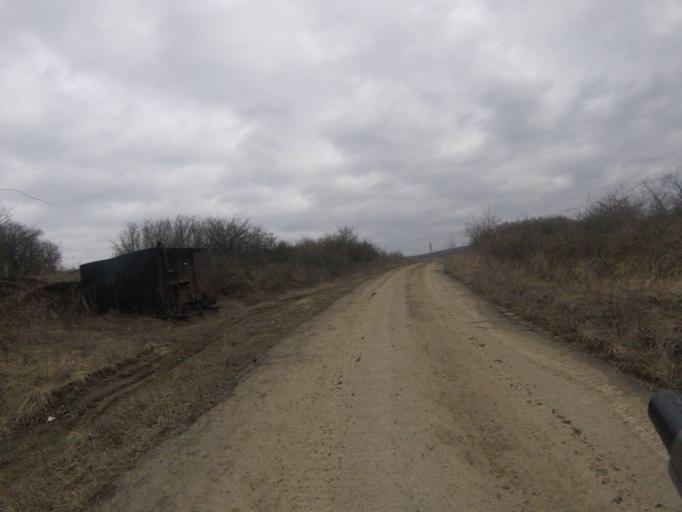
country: HU
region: Heves
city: Egerszalok
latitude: 47.8482
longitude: 20.3432
